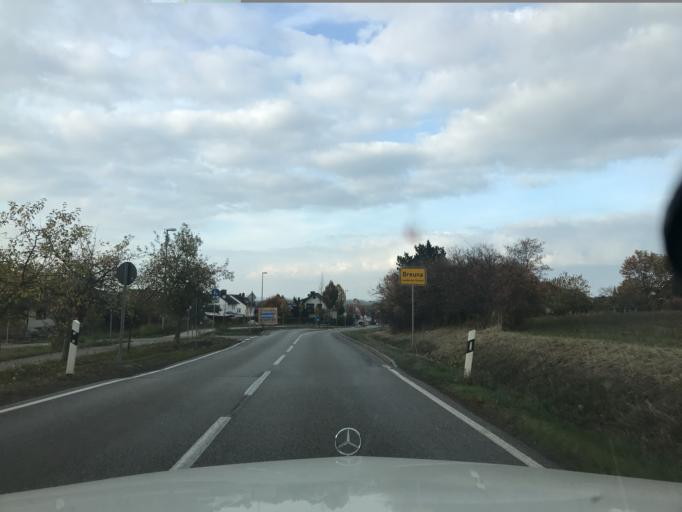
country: DE
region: Hesse
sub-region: Regierungsbezirk Kassel
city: Breuna
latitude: 51.4089
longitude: 9.1832
